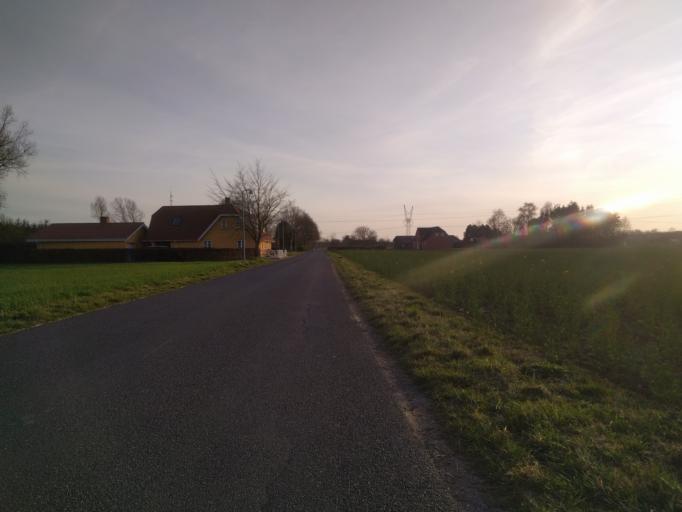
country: DK
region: South Denmark
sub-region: Odense Kommune
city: Bullerup
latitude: 55.4297
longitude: 10.5051
